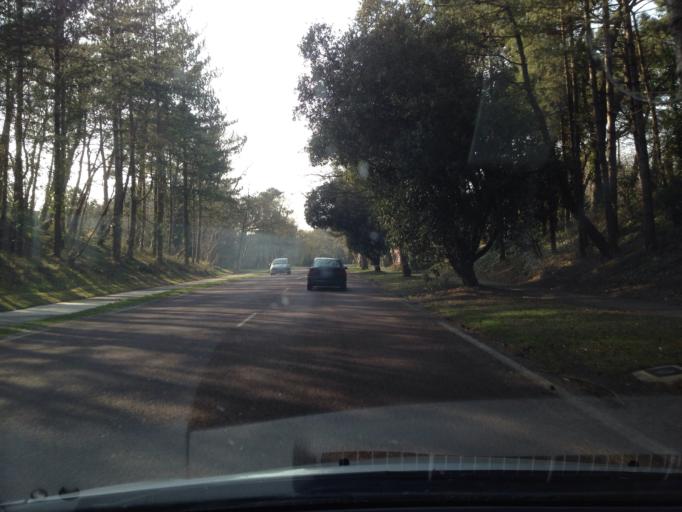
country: FR
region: Nord-Pas-de-Calais
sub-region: Departement du Pas-de-Calais
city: Le Touquet-Paris-Plage
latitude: 50.5091
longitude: 1.5995
